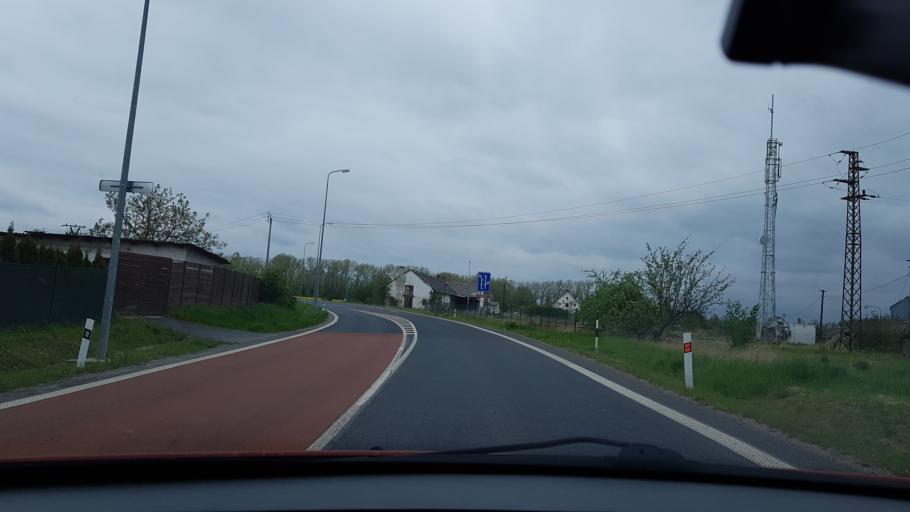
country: CZ
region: Olomoucky
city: Javornik
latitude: 50.3956
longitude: 17.0123
